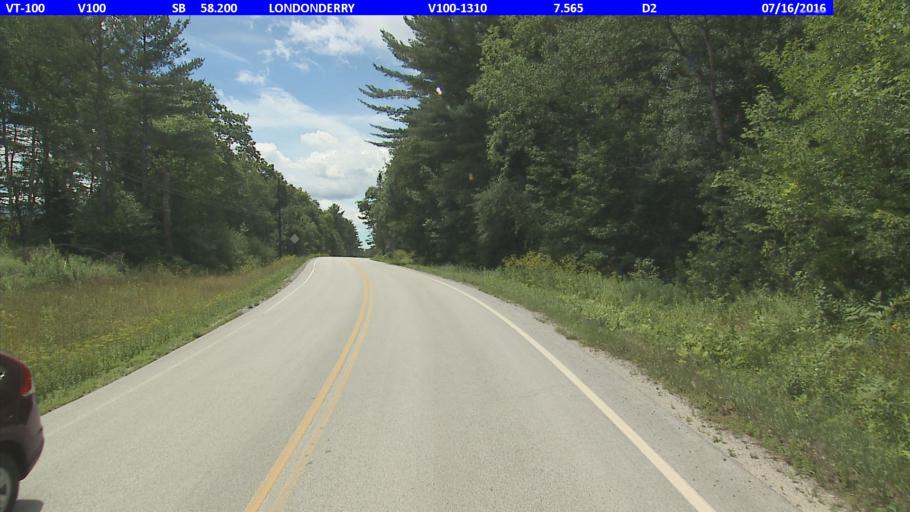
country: US
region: Vermont
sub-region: Windsor County
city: Chester
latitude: 43.2487
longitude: -72.7961
